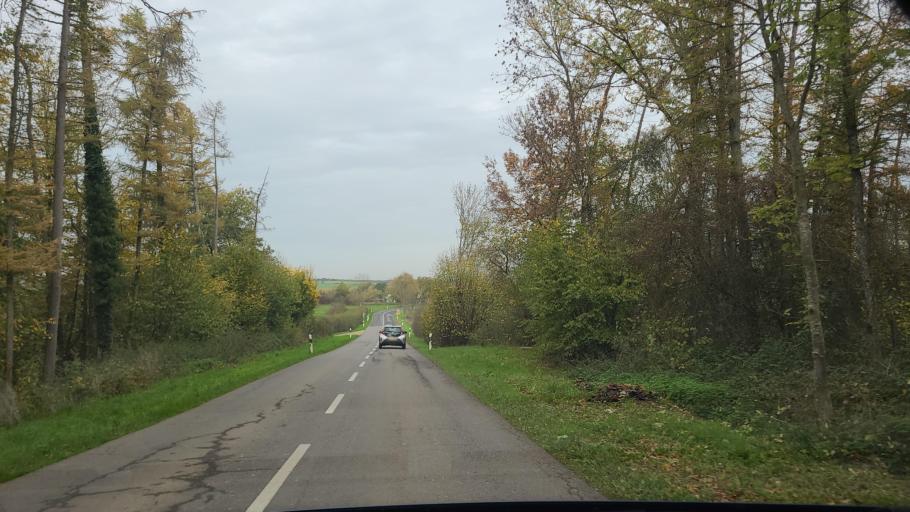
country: LU
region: Luxembourg
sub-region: Canton de Capellen
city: Dippach
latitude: 49.6097
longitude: 5.9920
